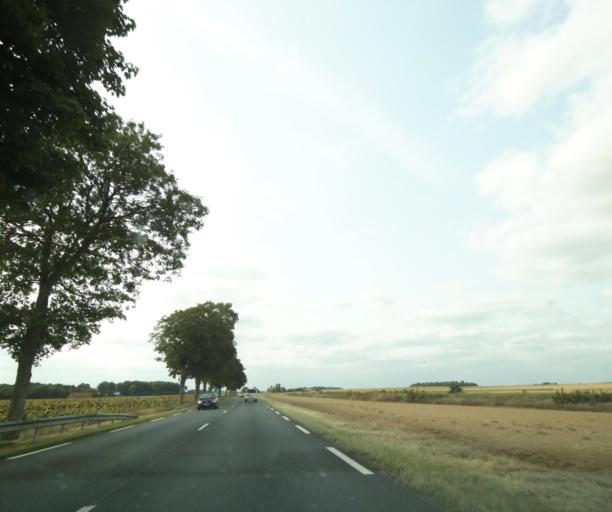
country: FR
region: Centre
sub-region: Departement d'Indre-et-Loire
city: Truyes
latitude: 47.2392
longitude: 0.8648
